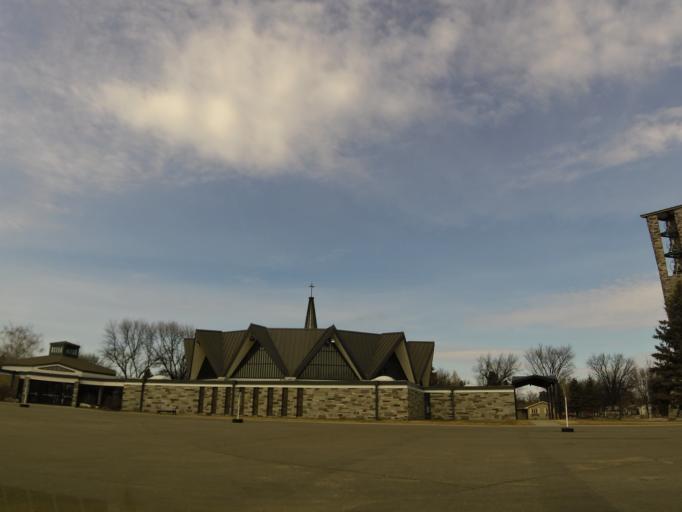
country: US
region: North Dakota
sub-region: Walsh County
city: Grafton
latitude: 48.4070
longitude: -97.4163
